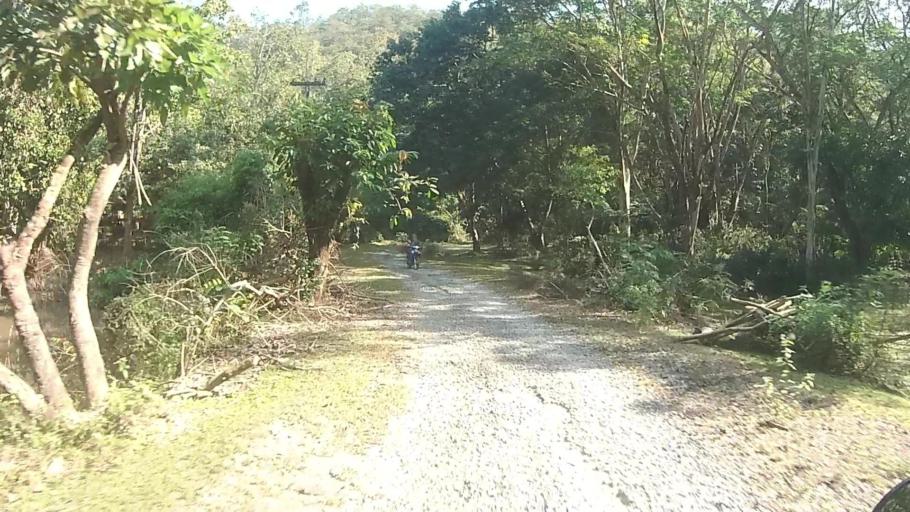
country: TH
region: Chiang Mai
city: Mae On
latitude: 18.9785
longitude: 99.2136
